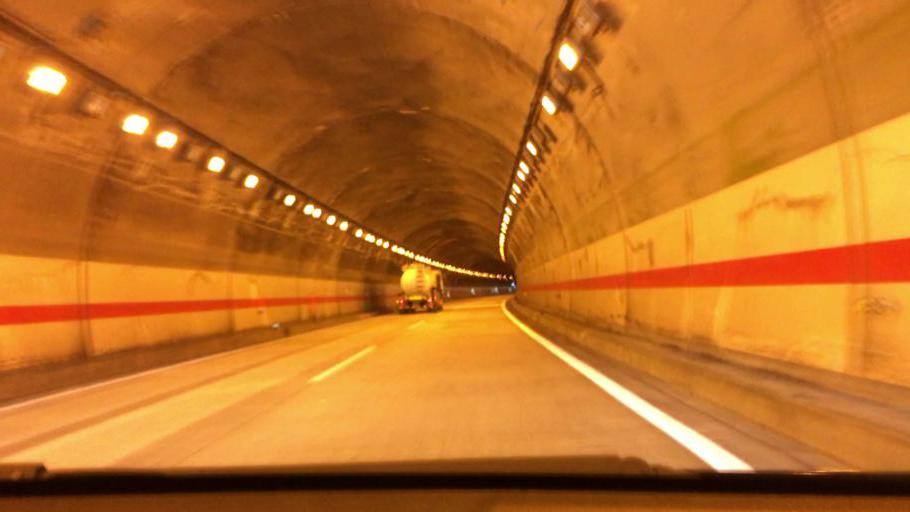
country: JP
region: Yamaguchi
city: Tokuyama
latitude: 34.0662
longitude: 131.6950
